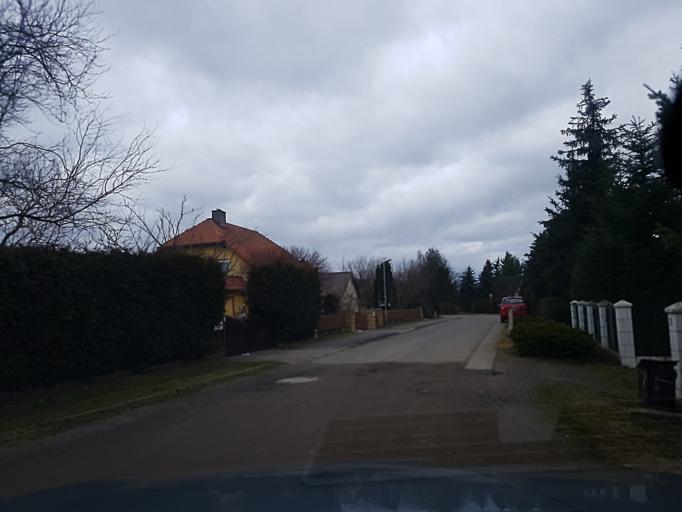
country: DE
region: Brandenburg
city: Bad Liebenwerda
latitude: 51.5445
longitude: 13.3630
